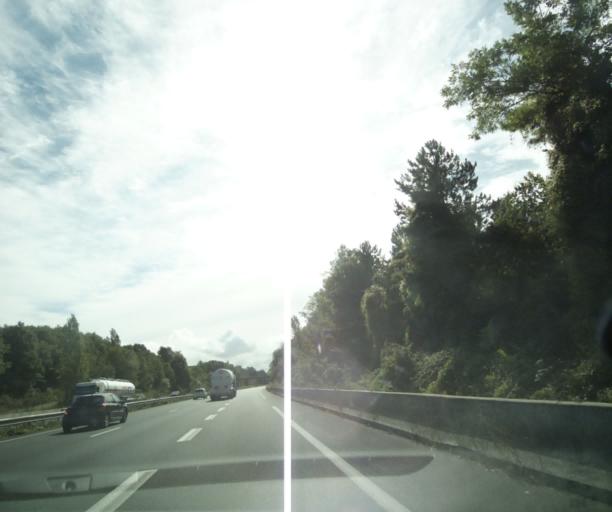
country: FR
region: Poitou-Charentes
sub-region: Departement de la Charente-Maritime
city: Pons
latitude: 45.6076
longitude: -0.5960
